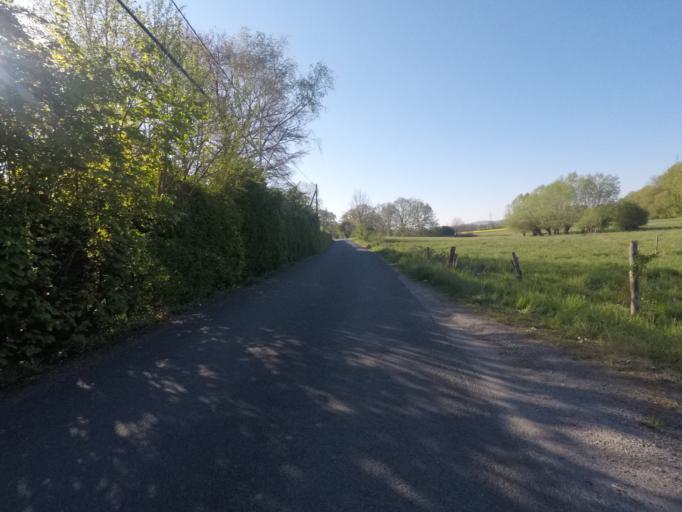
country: DE
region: North Rhine-Westphalia
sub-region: Regierungsbezirk Detmold
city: Bielefeld
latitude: 52.0490
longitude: 8.6111
